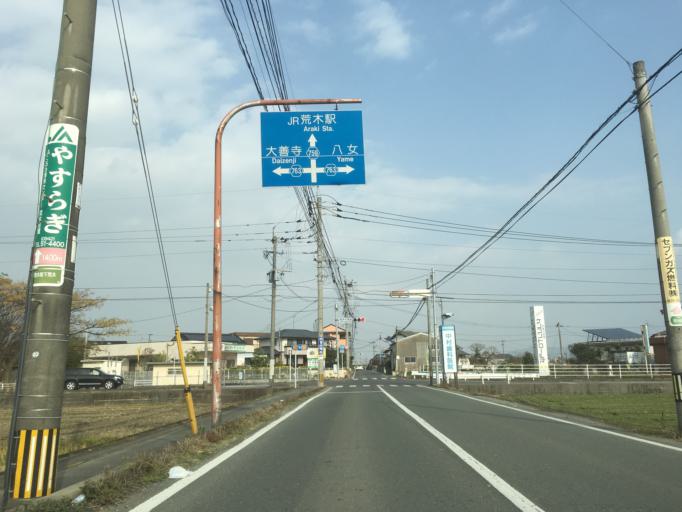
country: JP
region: Fukuoka
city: Kurume
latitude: 33.2701
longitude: 130.4914
